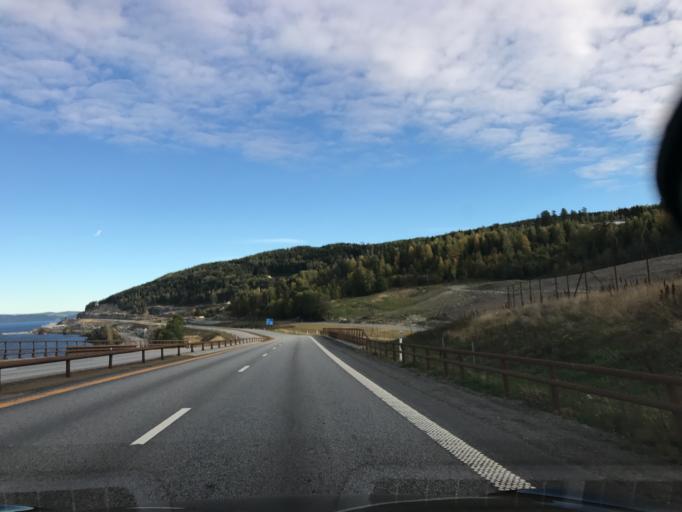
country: NO
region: Akershus
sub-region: Eidsvoll
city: Eidsvoll
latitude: 60.5038
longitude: 11.2400
